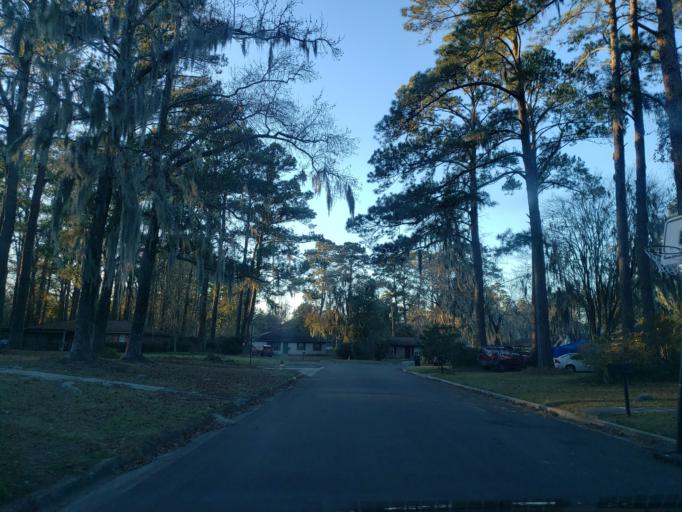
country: US
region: Georgia
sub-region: Chatham County
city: Isle of Hope
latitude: 31.9780
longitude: -81.0976
